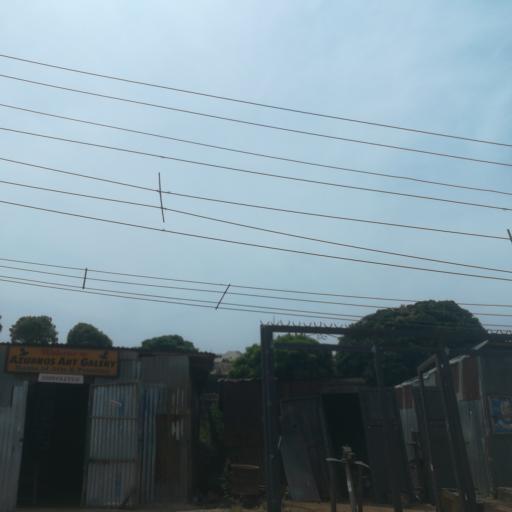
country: NG
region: Plateau
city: Jos
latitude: 9.9275
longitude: 8.8603
